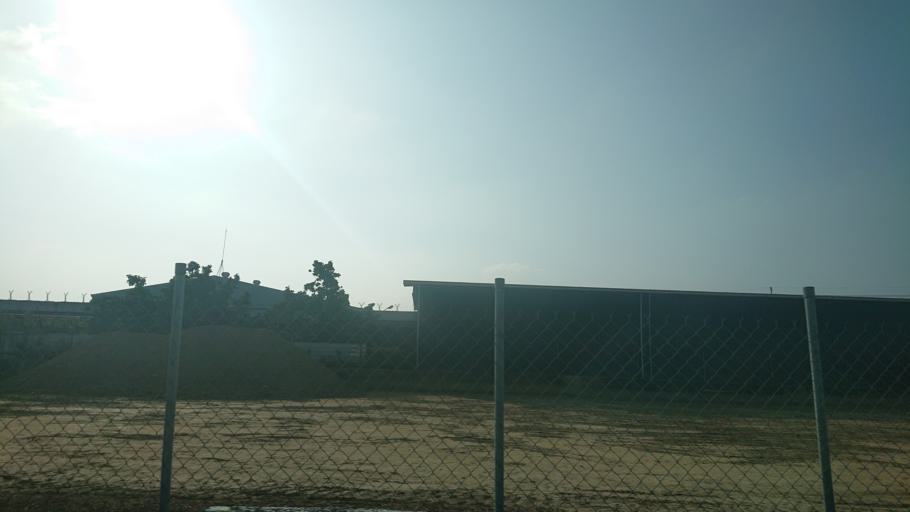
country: TW
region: Taiwan
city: Xinying
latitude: 23.2029
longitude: 120.2711
